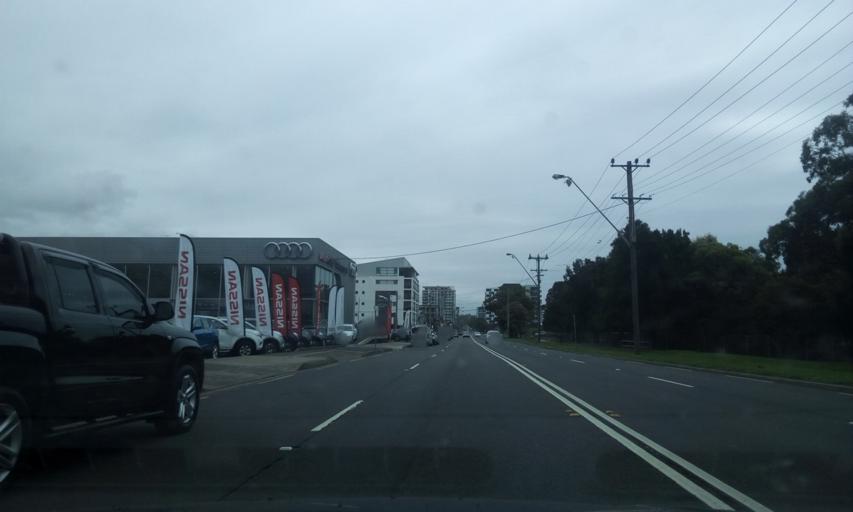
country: AU
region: New South Wales
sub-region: Wollongong
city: Wollongong
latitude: -34.4331
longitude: 150.8983
